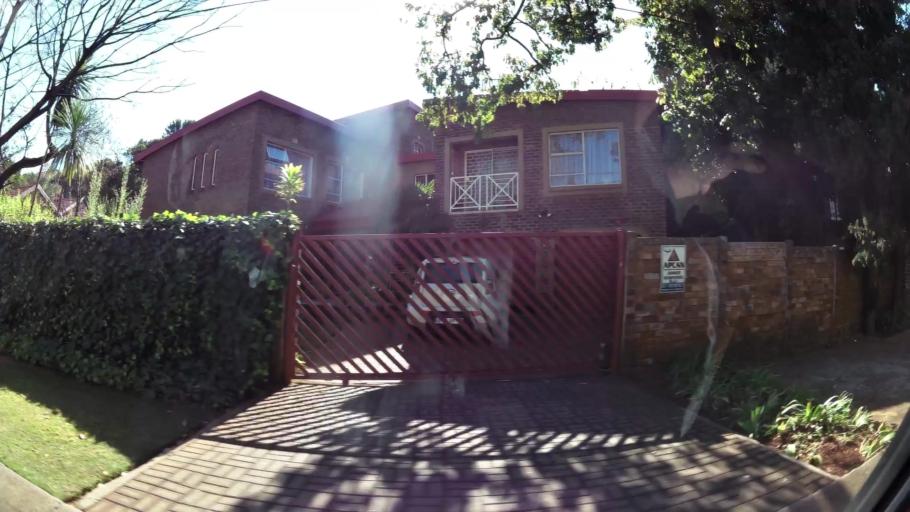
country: ZA
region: Gauteng
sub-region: City of Johannesburg Metropolitan Municipality
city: Roodepoort
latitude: -26.1182
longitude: 27.8569
